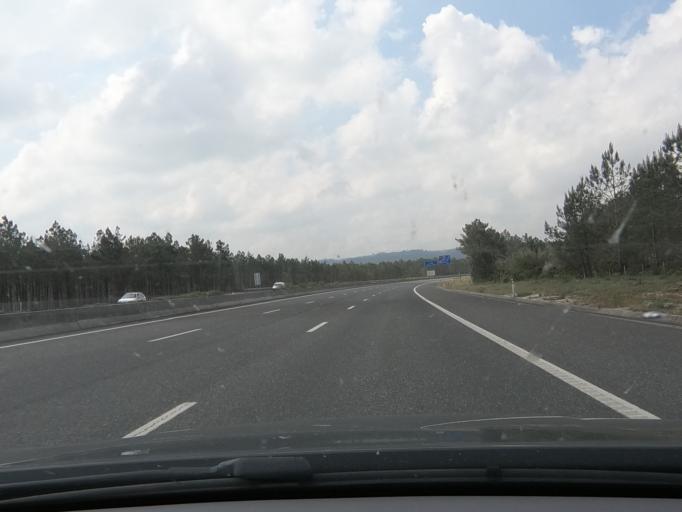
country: PT
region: Leiria
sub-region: Alcobaca
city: Alcobaca
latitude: 39.5988
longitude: -9.0009
